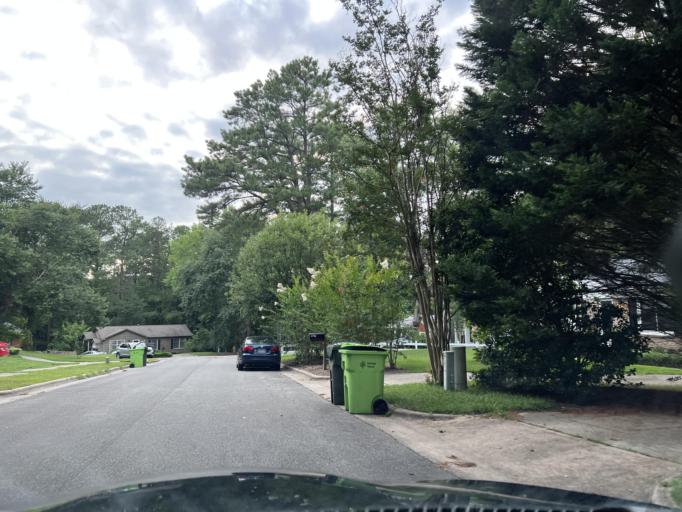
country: US
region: North Carolina
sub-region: Wake County
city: West Raleigh
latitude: 35.8644
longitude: -78.6559
